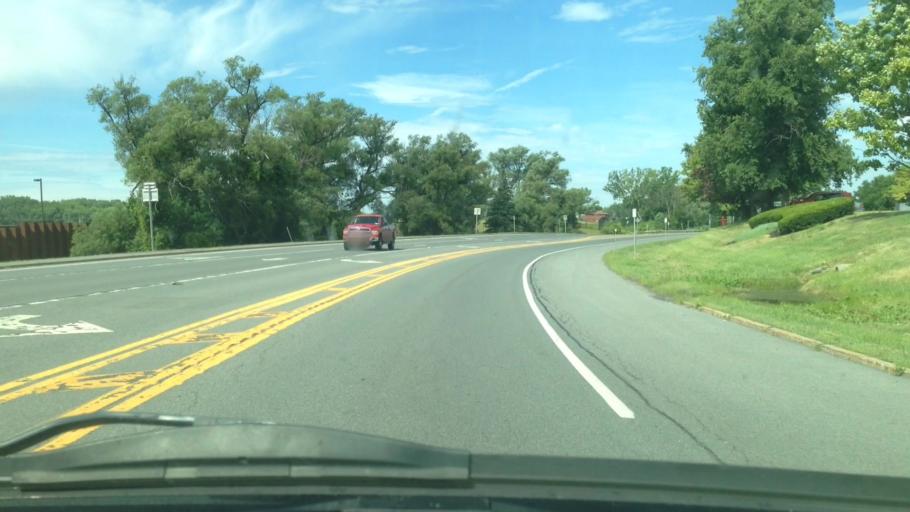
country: US
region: New York
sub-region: Onondaga County
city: East Syracuse
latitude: 43.0866
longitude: -76.0829
